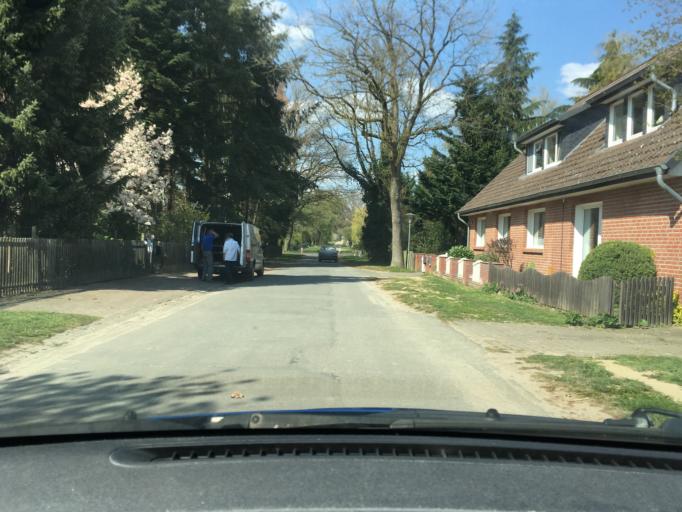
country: DE
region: Lower Saxony
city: Reinstorf
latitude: 53.2016
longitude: 10.5802
